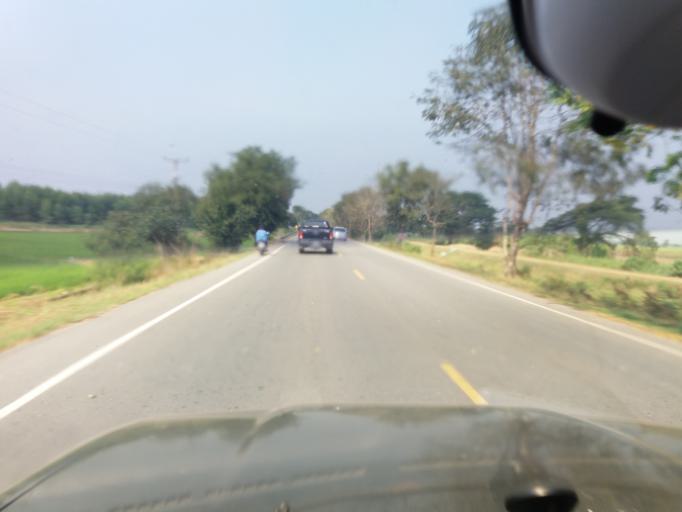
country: TH
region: Sing Buri
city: Bang Racham
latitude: 14.8813
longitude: 100.2777
